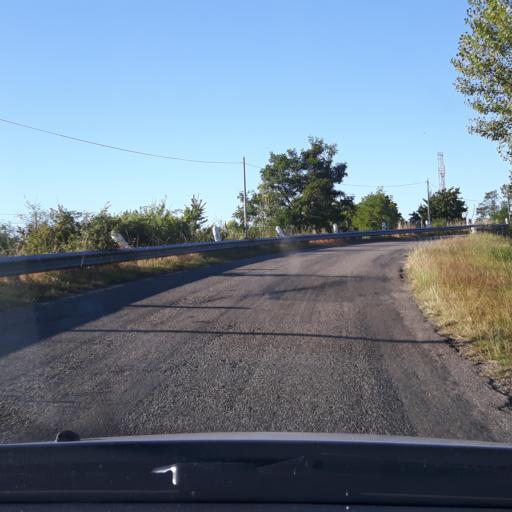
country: FR
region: Midi-Pyrenees
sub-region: Departement de la Haute-Garonne
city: Castelnau-d'Estretefonds
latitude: 43.7975
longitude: 1.3717
